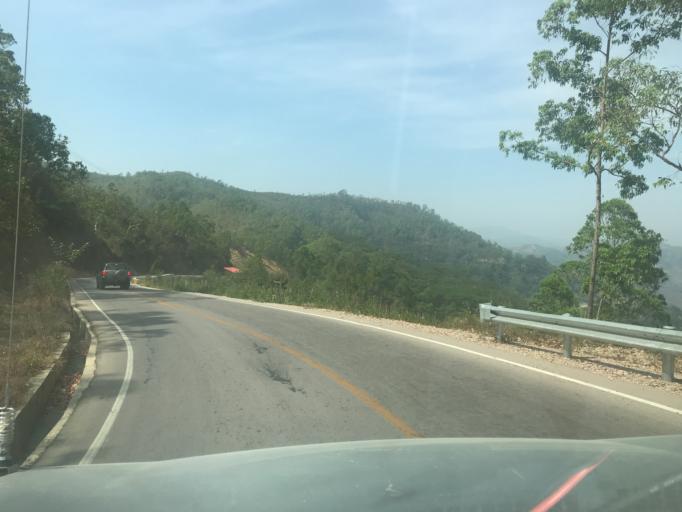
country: TL
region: Aileu
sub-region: Aileu Villa
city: Aileu
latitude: -8.6641
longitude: 125.5589
